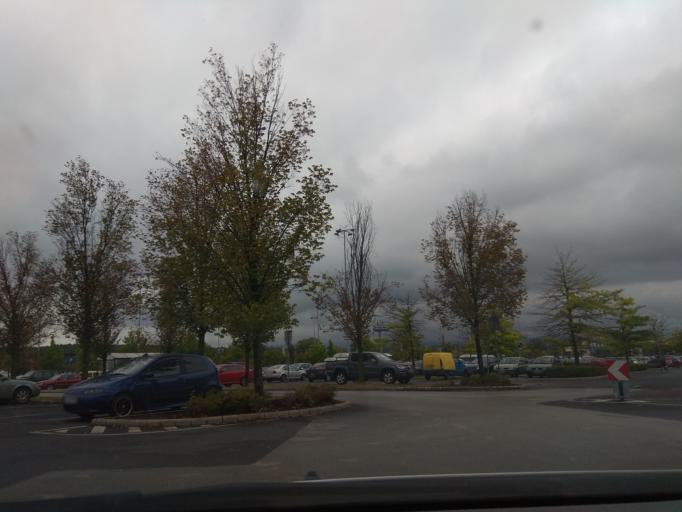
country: HU
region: Borsod-Abauj-Zemplen
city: Miskolc
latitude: 48.0576
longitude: 20.8016
